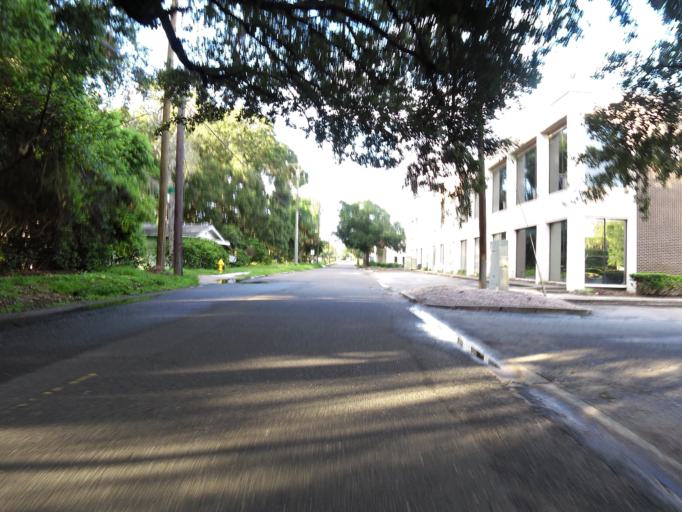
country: US
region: Florida
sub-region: Duval County
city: Jacksonville
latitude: 30.3021
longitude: -81.6209
